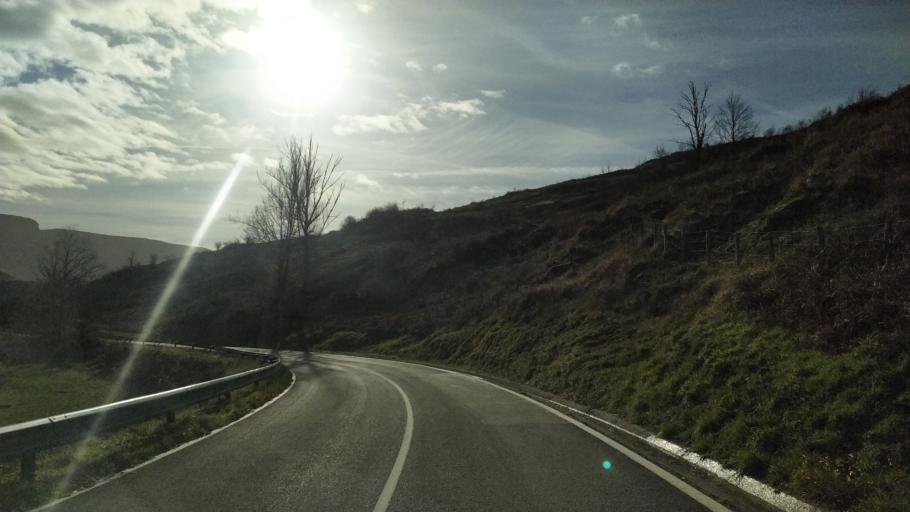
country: ES
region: Cantabria
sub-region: Provincia de Cantabria
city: San Martin de Elines
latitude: 42.8431
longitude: -3.9122
